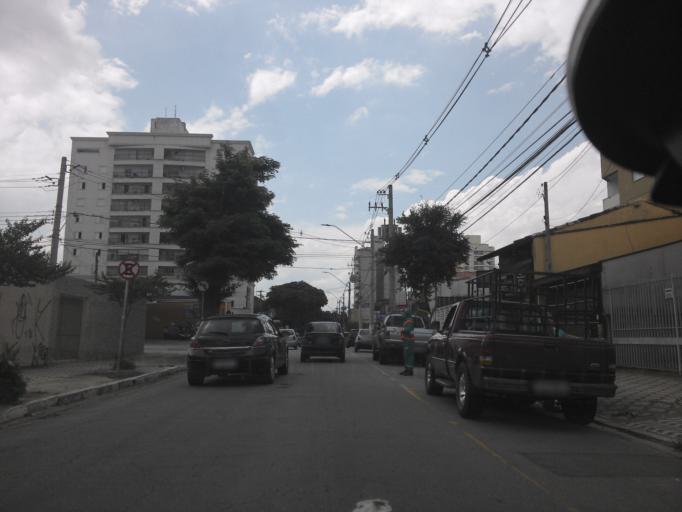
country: BR
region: Sao Paulo
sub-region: Taubate
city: Taubate
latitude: -23.0280
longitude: -45.5606
